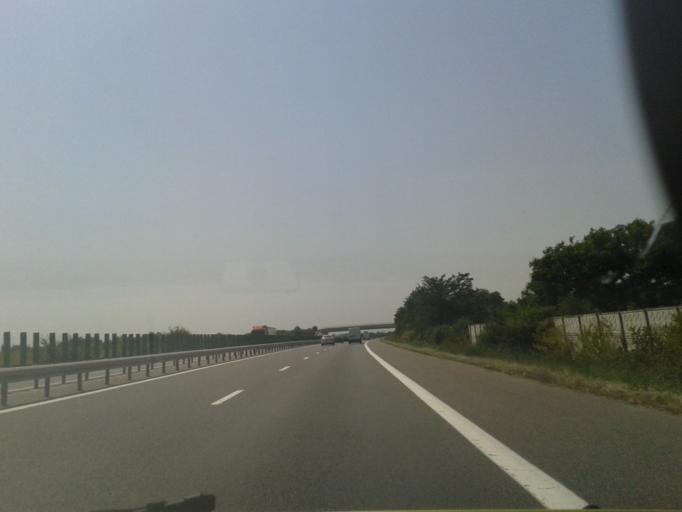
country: RO
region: Calarasi
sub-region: Comuna Sarulesti
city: Sarulesti-Gara
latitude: 44.4393
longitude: 26.6560
